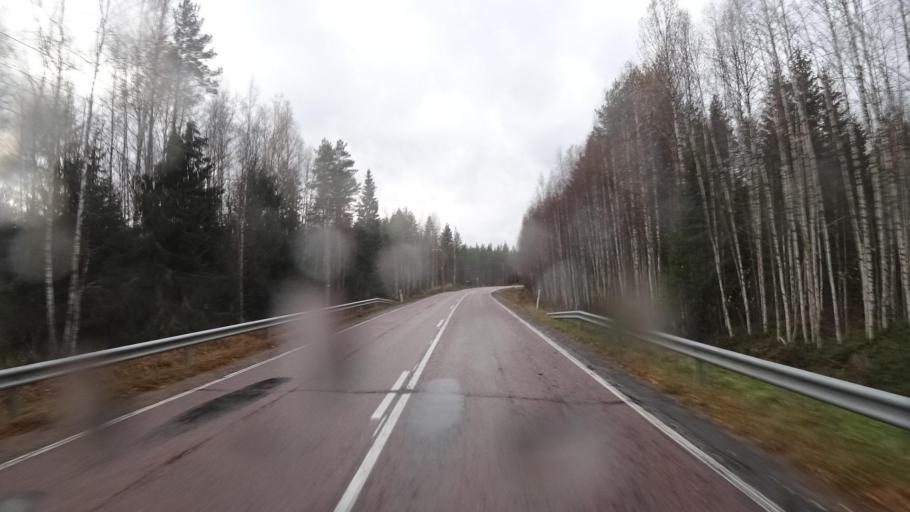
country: FI
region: Southern Savonia
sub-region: Mikkeli
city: Kangasniemi
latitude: 62.0739
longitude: 26.6855
